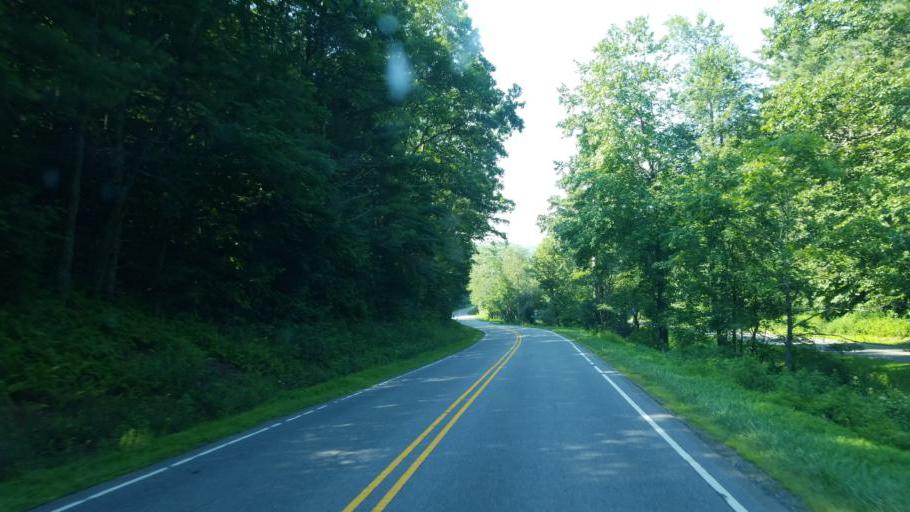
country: US
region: North Carolina
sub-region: Avery County
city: Newland
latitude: 35.9964
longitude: -81.8905
